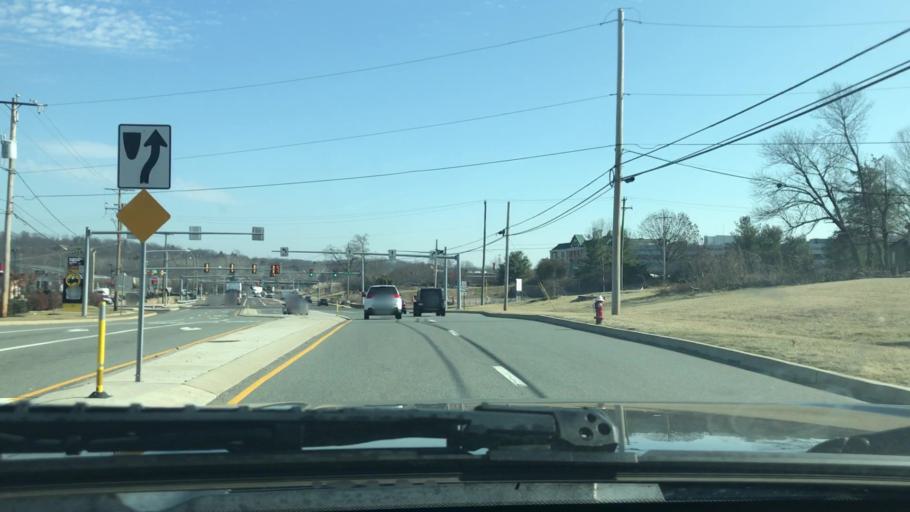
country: US
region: Pennsylvania
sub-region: Montgomery County
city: Audubon
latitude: 40.1330
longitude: -75.4540
